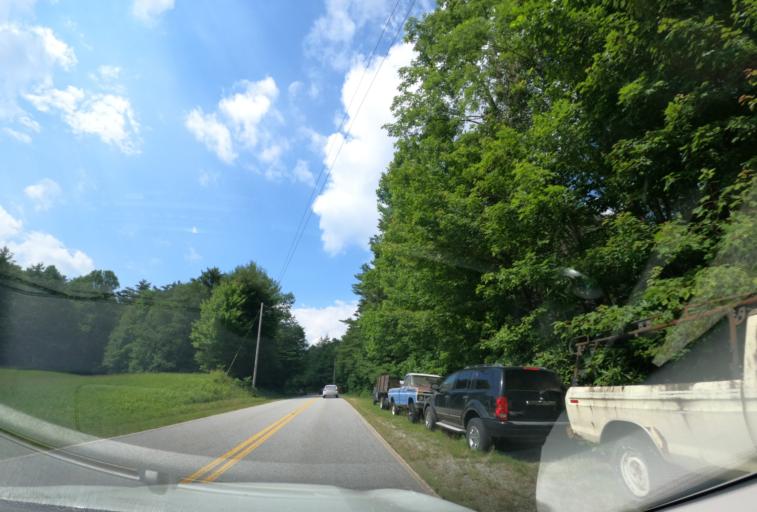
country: US
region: North Carolina
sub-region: Jackson County
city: Cullowhee
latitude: 35.0650
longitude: -83.0069
